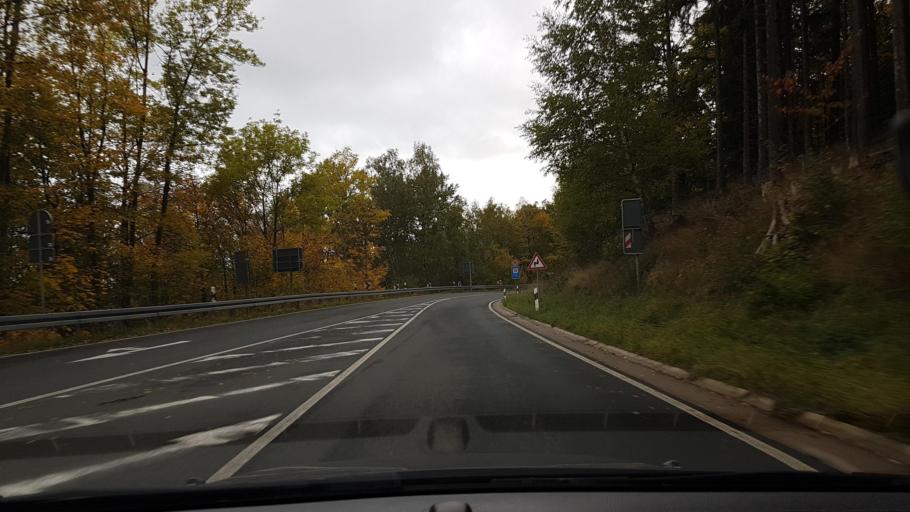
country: DE
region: Lower Saxony
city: Bad Grund
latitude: 51.8094
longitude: 10.2486
